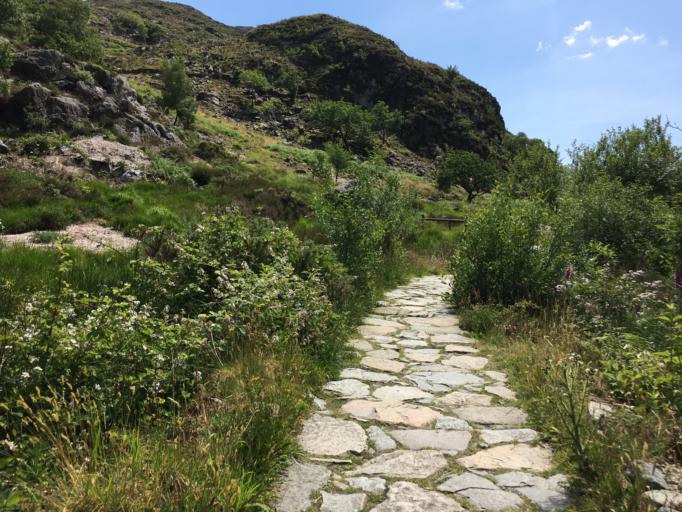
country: GB
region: Wales
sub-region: Gwynedd
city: Penrhyndeudraeth
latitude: 53.0137
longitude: -4.0987
